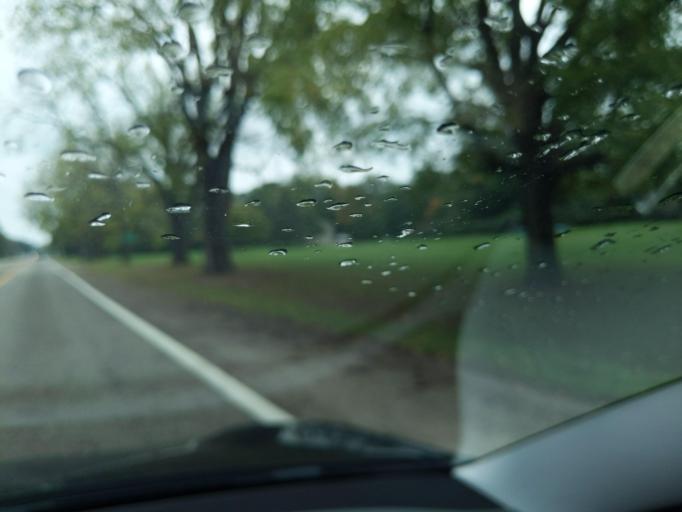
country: US
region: Michigan
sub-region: Eaton County
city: Charlotte
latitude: 42.5531
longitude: -84.8142
